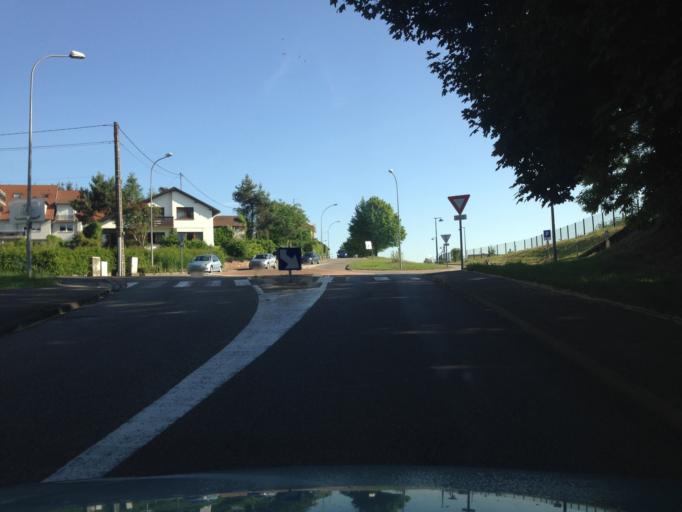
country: FR
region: Alsace
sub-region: Departement du Bas-Rhin
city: Ingwiller
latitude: 48.8694
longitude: 7.4759
